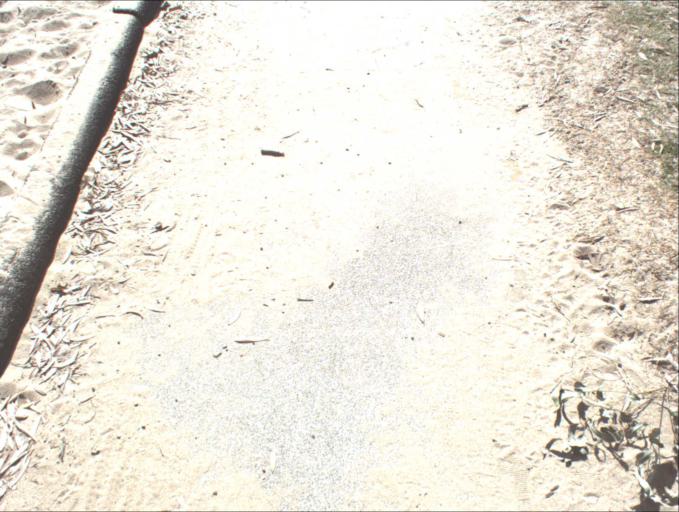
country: AU
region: Queensland
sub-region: Logan
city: Beenleigh
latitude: -27.6921
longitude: 153.2085
